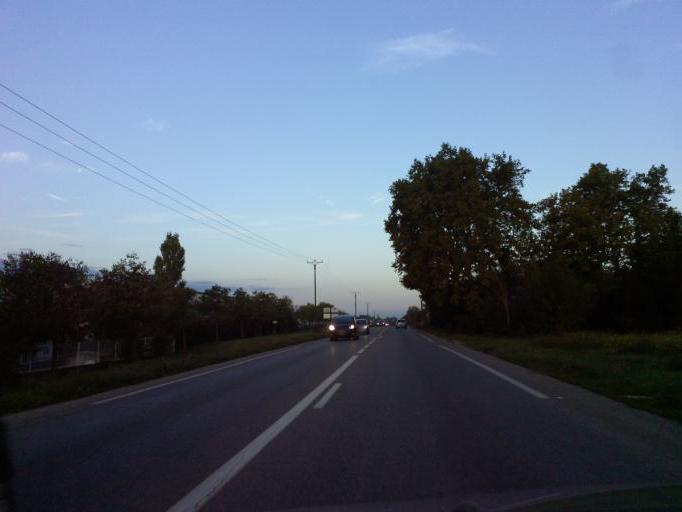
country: FR
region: Provence-Alpes-Cote d'Azur
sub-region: Departement des Bouches-du-Rhone
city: Saint-Cannat
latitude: 43.6144
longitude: 5.3203
